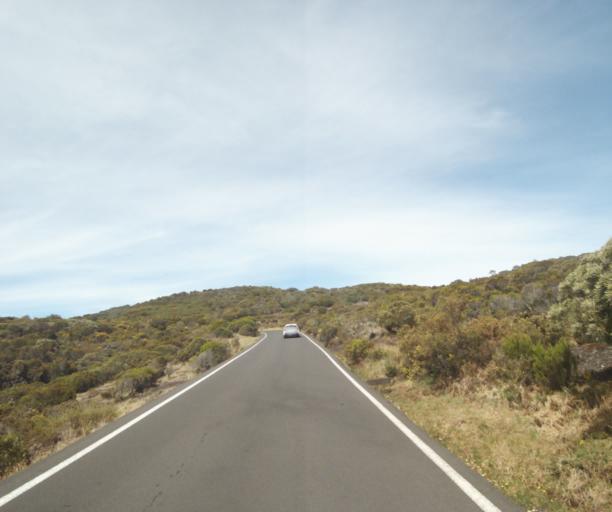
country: RE
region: Reunion
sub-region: Reunion
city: Trois-Bassins
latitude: -21.0707
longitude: 55.3841
